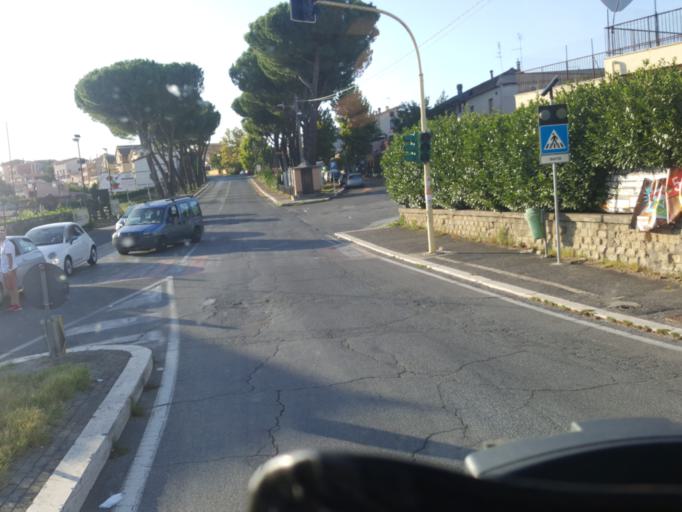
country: IT
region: Latium
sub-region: Citta metropolitana di Roma Capitale
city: Bivio di Capanelle
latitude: 42.1213
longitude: 12.5910
